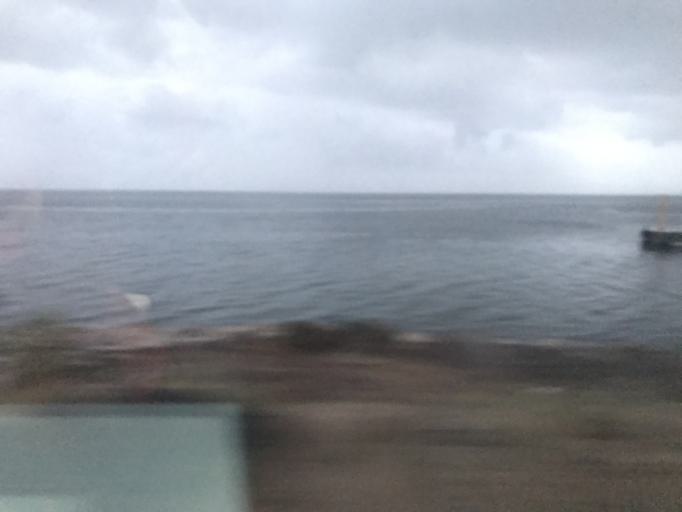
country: TR
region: Kocaeli
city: Tavsancil
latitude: 40.7677
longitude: 29.5739
